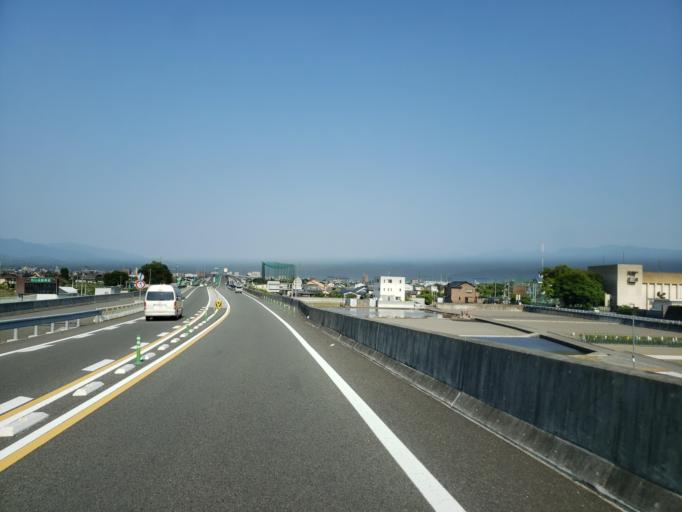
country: JP
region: Ehime
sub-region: Shikoku-chuo Shi
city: Matsuyama
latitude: 33.8025
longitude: 132.7654
